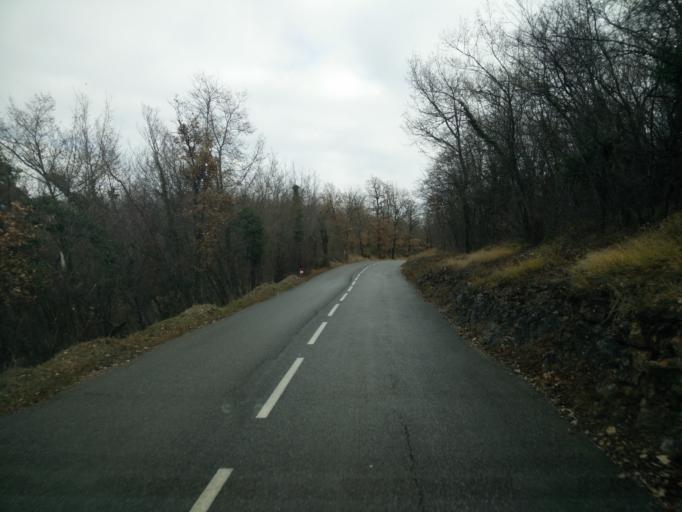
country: FR
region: Provence-Alpes-Cote d'Azur
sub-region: Departement des Alpes-Maritimes
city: Le Broc
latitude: 43.8243
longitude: 7.1503
